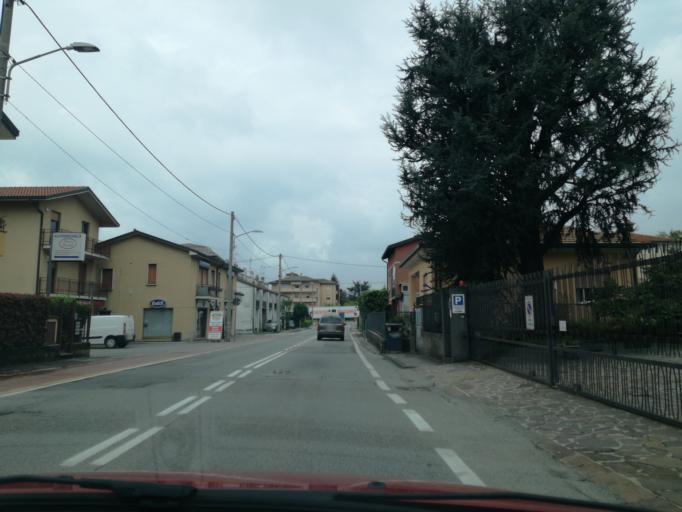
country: IT
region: Lombardy
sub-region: Provincia di Lecco
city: Cernusco Lombardone
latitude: 45.6975
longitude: 9.4082
